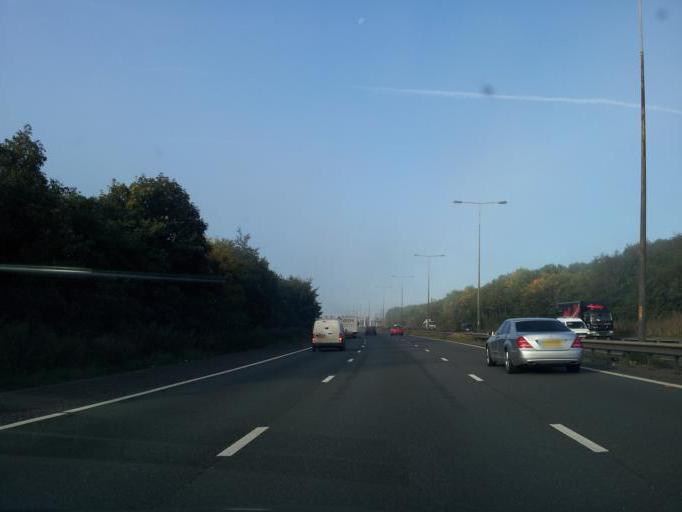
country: GB
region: England
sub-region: City and Borough of Leeds
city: Gildersome
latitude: 53.7476
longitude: -1.6410
